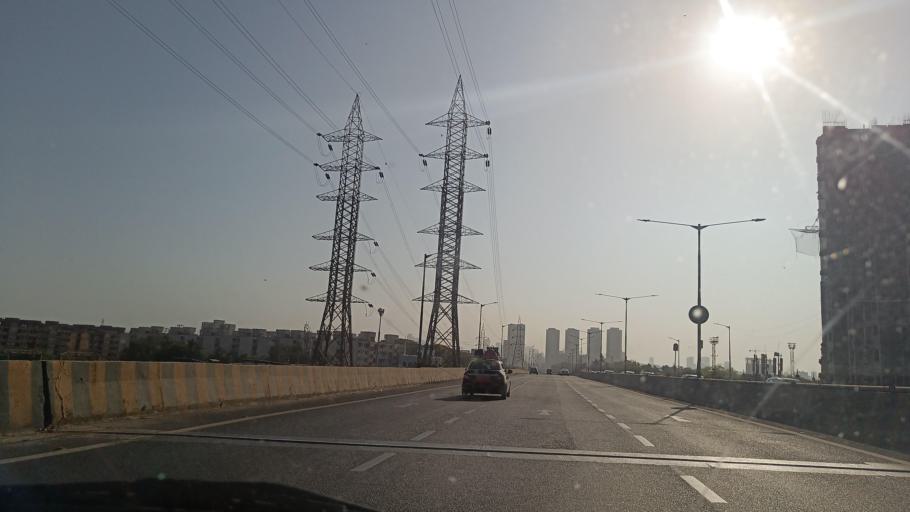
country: IN
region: Maharashtra
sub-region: Mumbai Suburban
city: Mumbai
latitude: 19.0330
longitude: 72.8964
